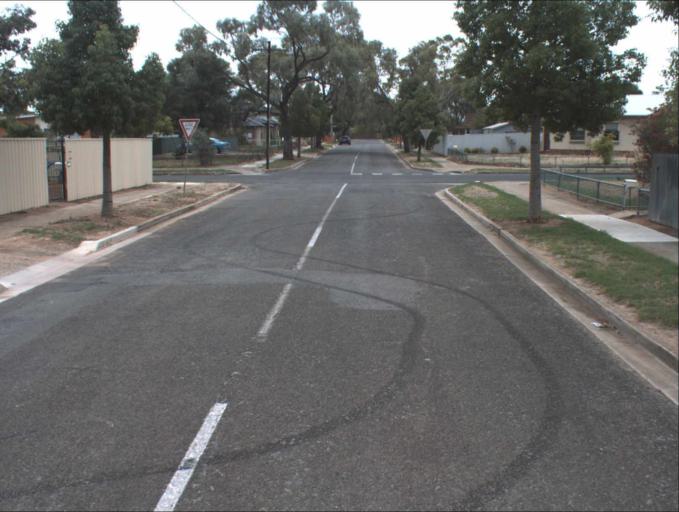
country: AU
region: South Australia
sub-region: Port Adelaide Enfield
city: Enfield
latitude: -34.8537
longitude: 138.6213
